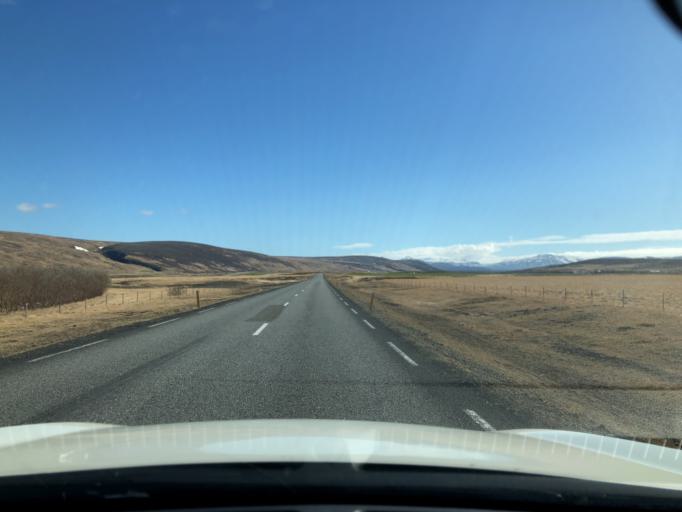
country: IS
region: South
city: Hveragerdi
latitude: 64.6986
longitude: -21.2304
